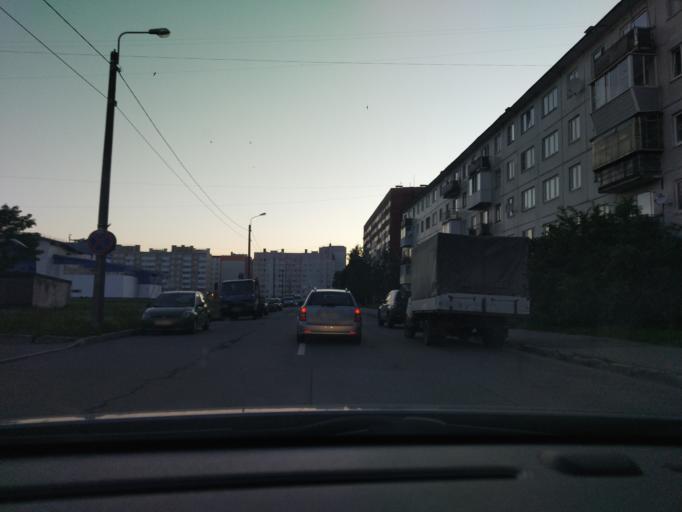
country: RU
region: St.-Petersburg
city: Krasnoye Selo
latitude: 59.7427
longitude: 30.0898
